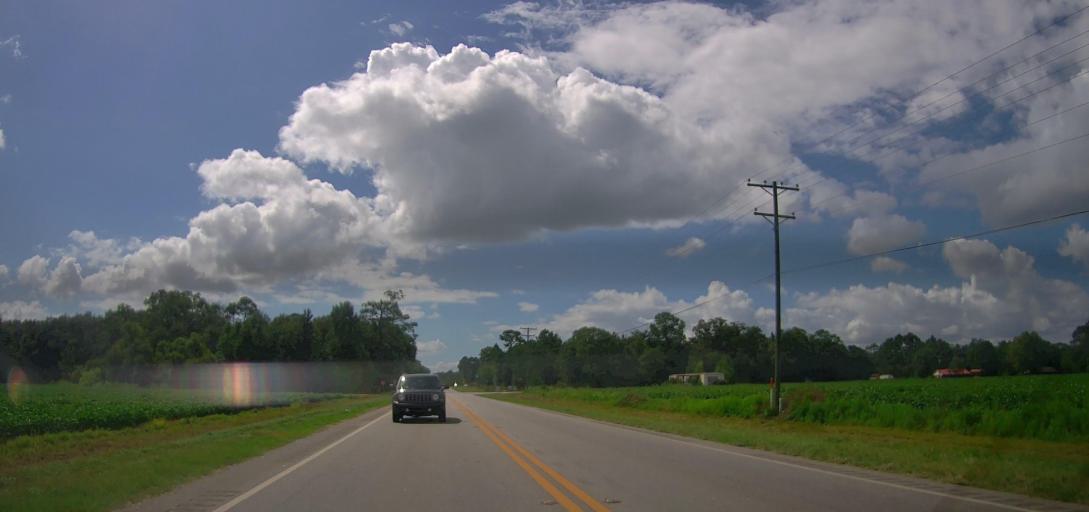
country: US
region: Georgia
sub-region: Coffee County
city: Broxton
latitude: 31.5542
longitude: -82.9625
